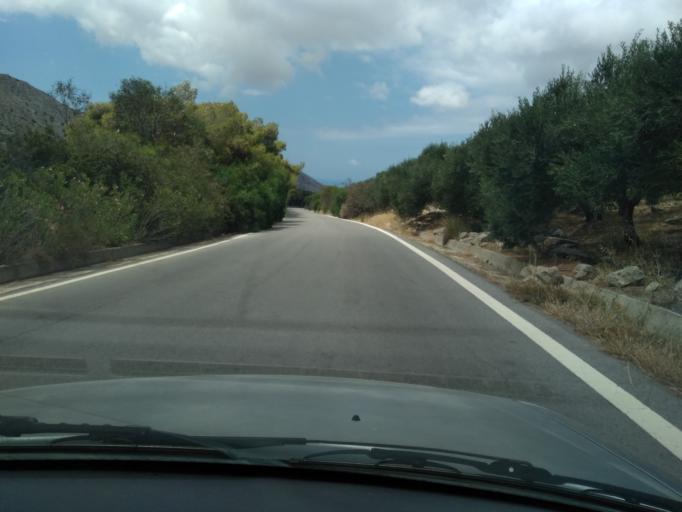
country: GR
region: Crete
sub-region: Nomos Lasithiou
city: Makry-Gialos
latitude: 35.0636
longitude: 26.0448
